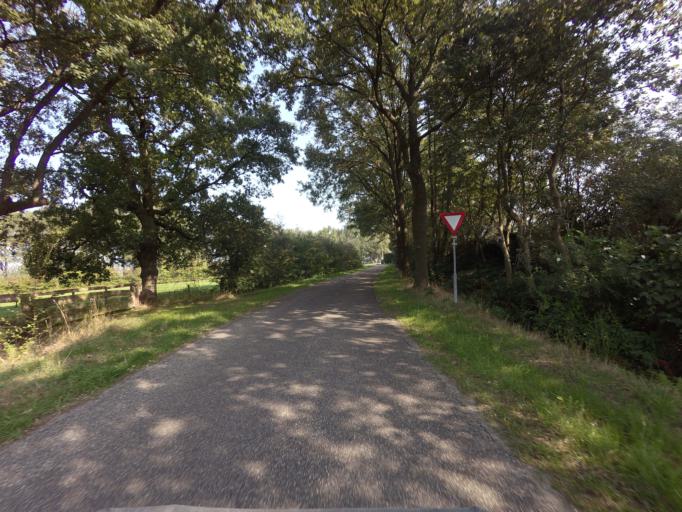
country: NL
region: Drenthe
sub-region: Gemeente Tynaarlo
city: Vries
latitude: 53.1379
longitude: 6.5305
